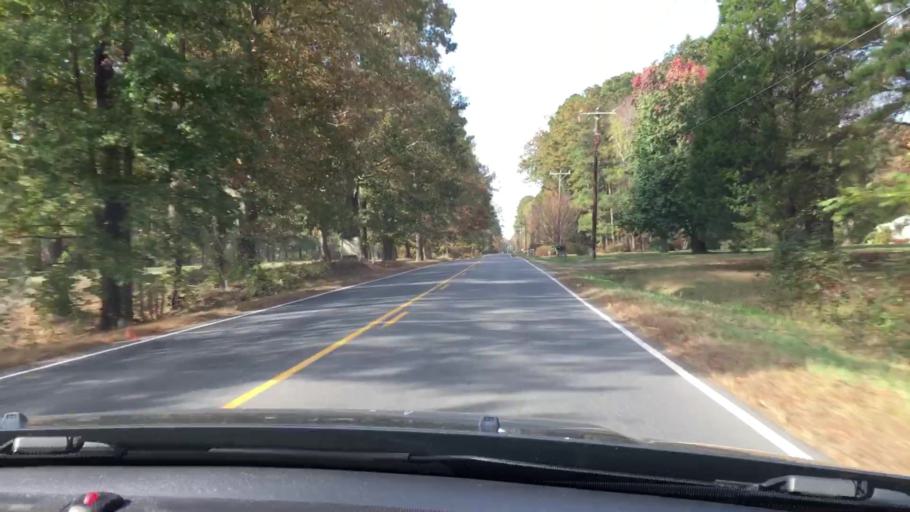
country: US
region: Virginia
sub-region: King William County
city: West Point
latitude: 37.5624
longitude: -76.8249
